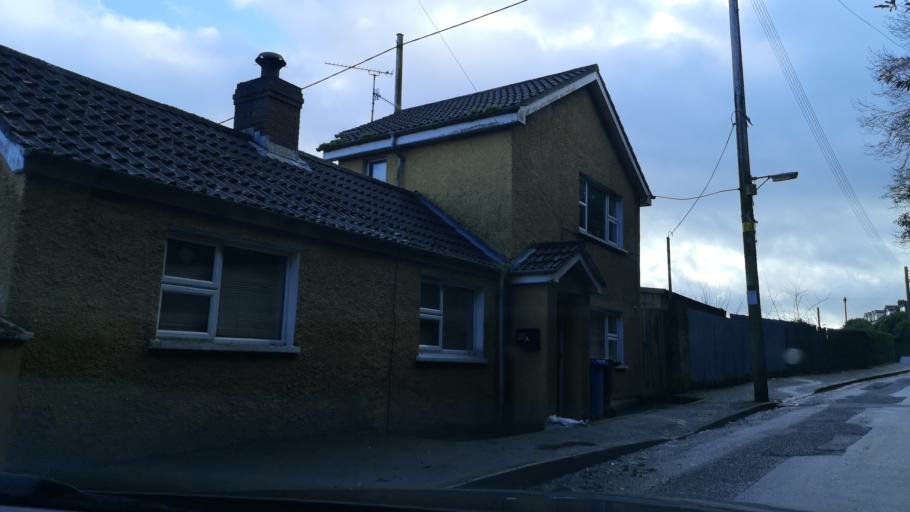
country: GB
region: Northern Ireland
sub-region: Newry and Mourne District
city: Newry
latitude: 54.1757
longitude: -6.3480
